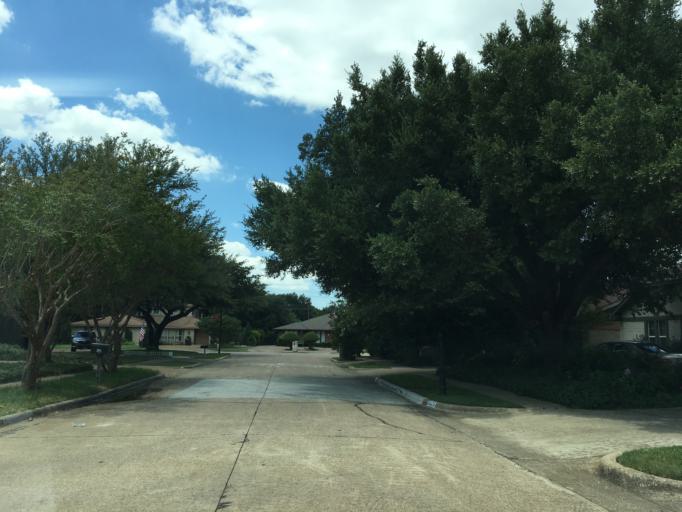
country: US
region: Texas
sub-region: Dallas County
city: Addison
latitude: 32.9331
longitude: -96.8545
